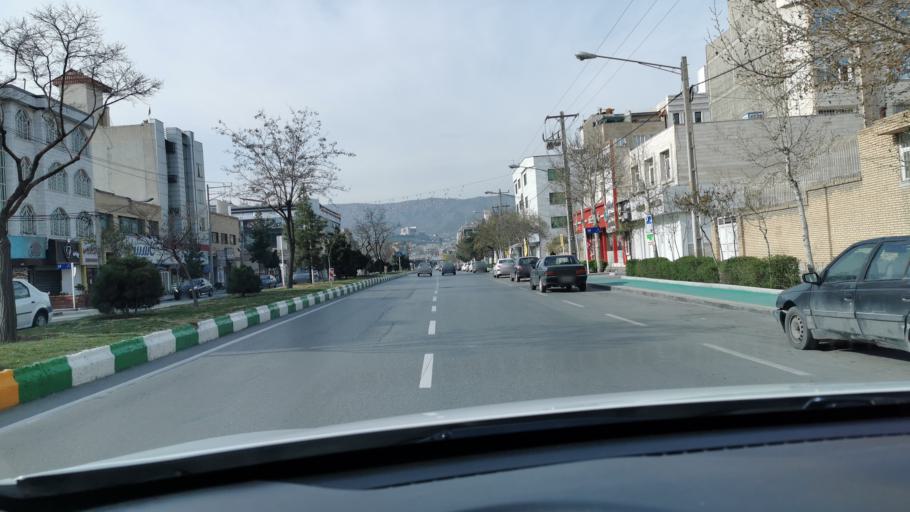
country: IR
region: Razavi Khorasan
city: Mashhad
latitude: 36.3178
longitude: 59.5107
